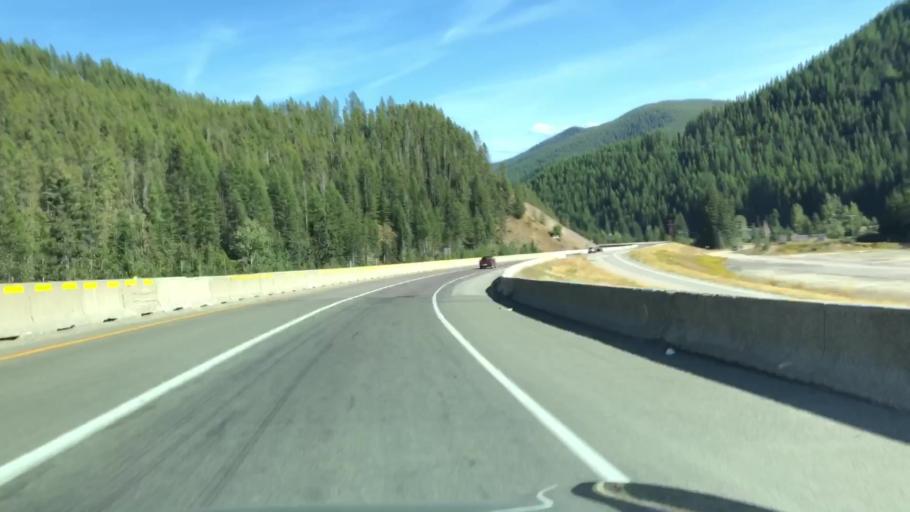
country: US
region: Montana
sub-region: Sanders County
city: Thompson Falls
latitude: 47.4219
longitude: -115.6068
